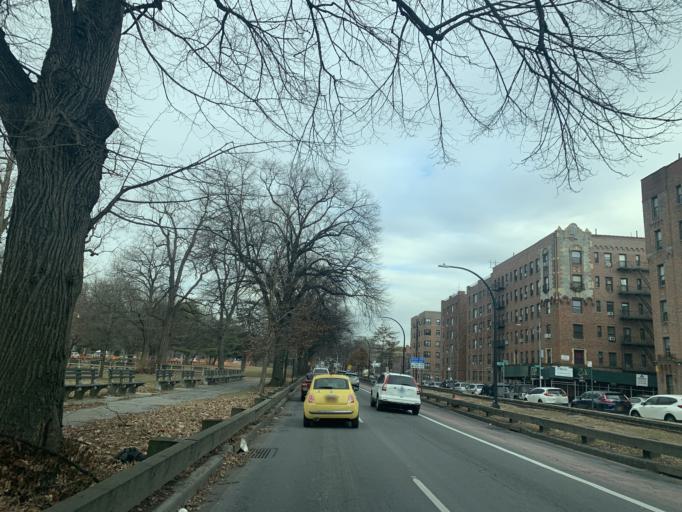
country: US
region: New York
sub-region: Bronx
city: The Bronx
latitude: 40.8569
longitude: -73.8646
